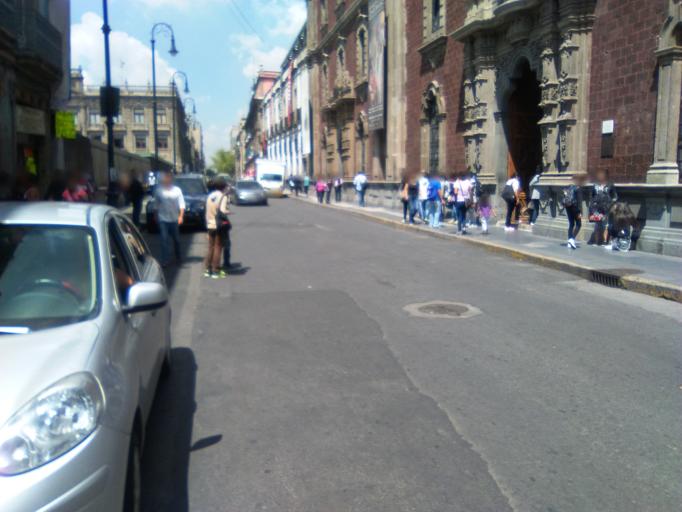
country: MX
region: Mexico City
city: Mexico City
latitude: 19.4356
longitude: -99.1309
